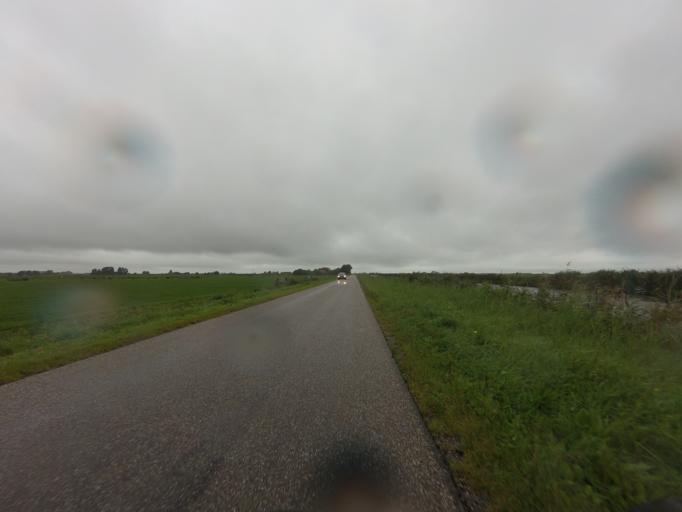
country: NL
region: Friesland
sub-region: Sudwest Fryslan
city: Workum
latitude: 52.9860
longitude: 5.4709
